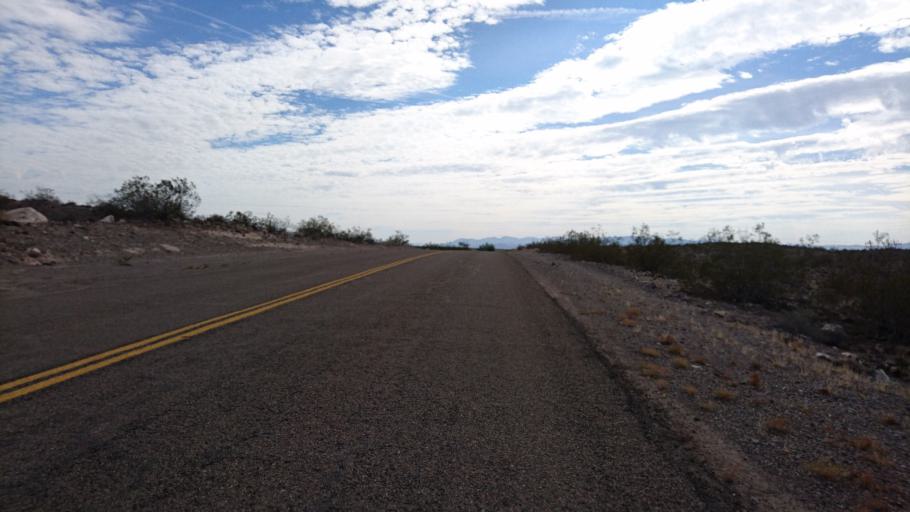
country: US
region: Arizona
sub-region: Mohave County
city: Mohave Valley
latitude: 34.8780
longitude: -114.4362
